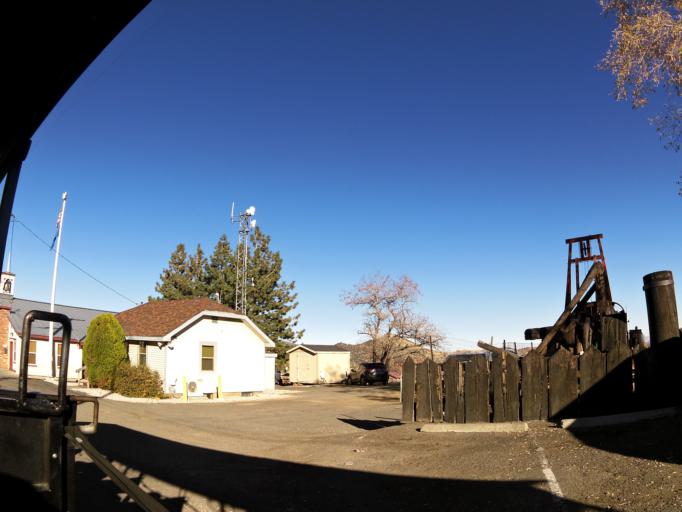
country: US
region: Nevada
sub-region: Storey County
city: Virginia City
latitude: 39.3125
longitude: -119.6489
